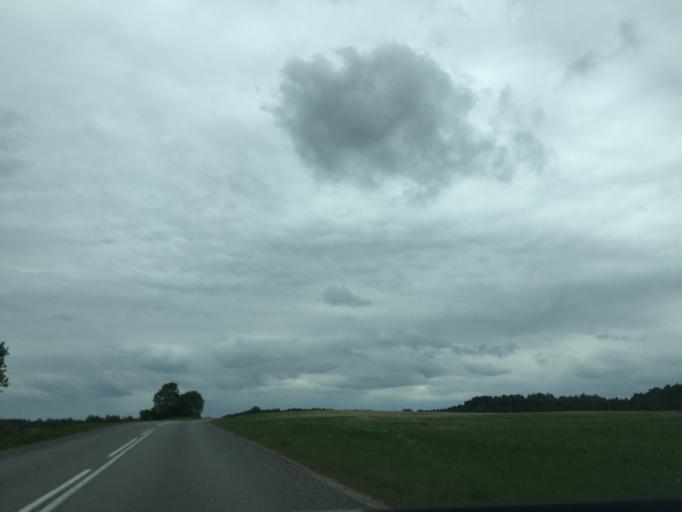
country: LV
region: Aglona
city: Aglona
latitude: 56.1329
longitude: 27.0731
